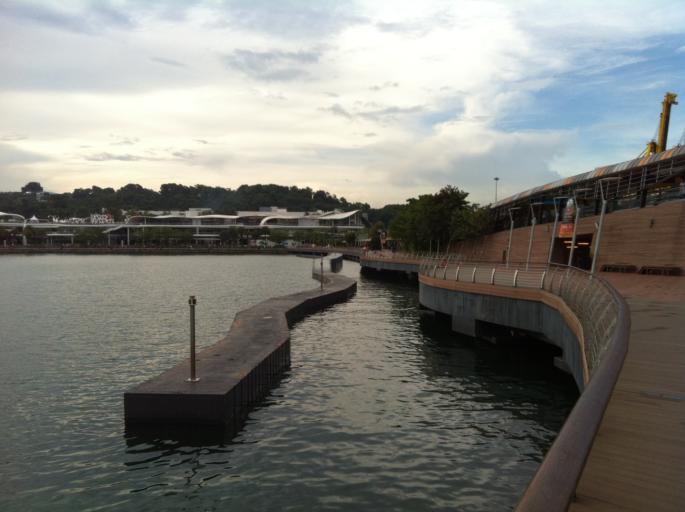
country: SG
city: Singapore
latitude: 1.2604
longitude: 103.8233
